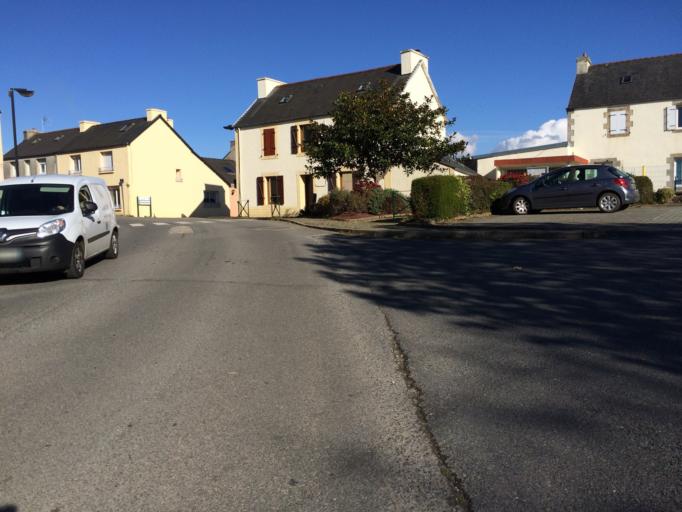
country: FR
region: Brittany
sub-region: Departement du Finistere
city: Saint-Urbain
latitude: 48.4009
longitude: -4.2280
